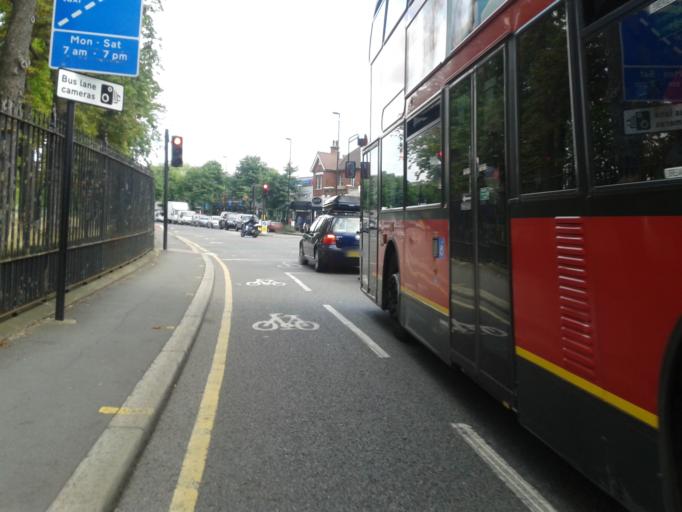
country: GB
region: England
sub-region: Greater London
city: Brixton
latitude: 51.4501
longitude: -0.1009
